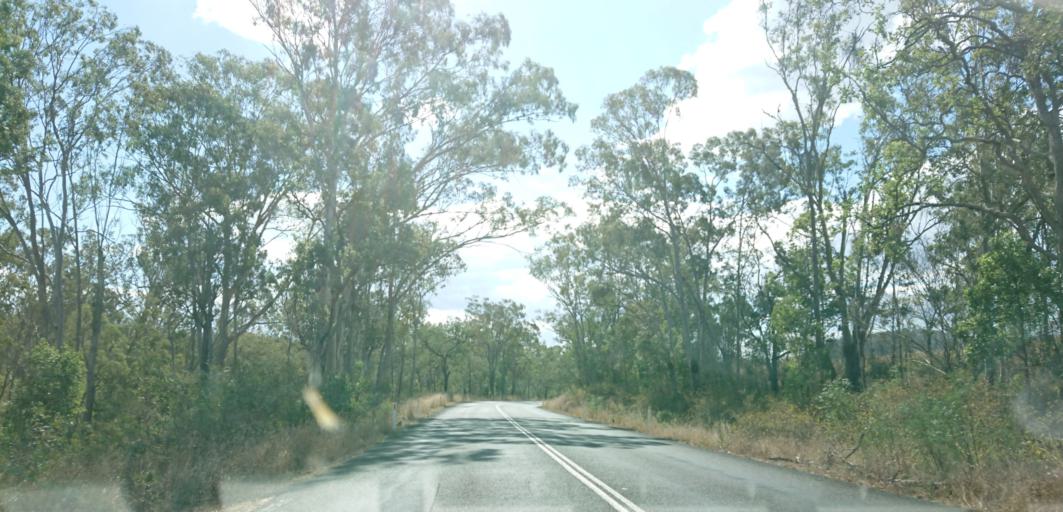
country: AU
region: Queensland
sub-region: Toowoomba
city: Top Camp
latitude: -27.8137
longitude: 152.1066
